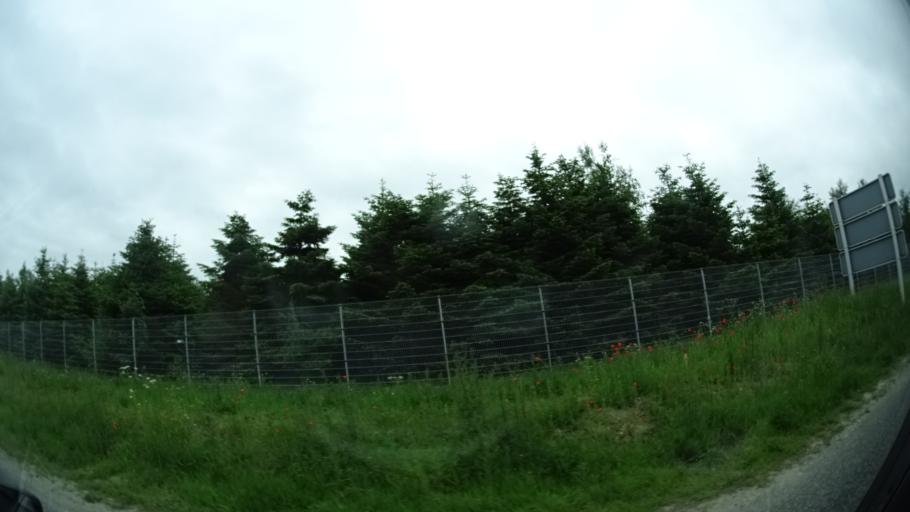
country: DK
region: Central Jutland
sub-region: Arhus Kommune
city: Kolt
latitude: 56.1089
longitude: 10.0486
